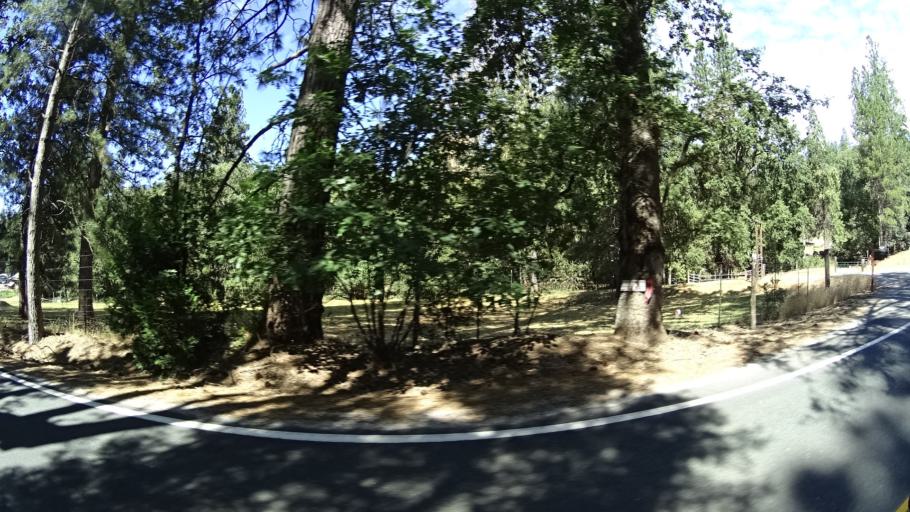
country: US
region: California
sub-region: Amador County
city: Pioneer
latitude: 38.3500
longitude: -120.5827
